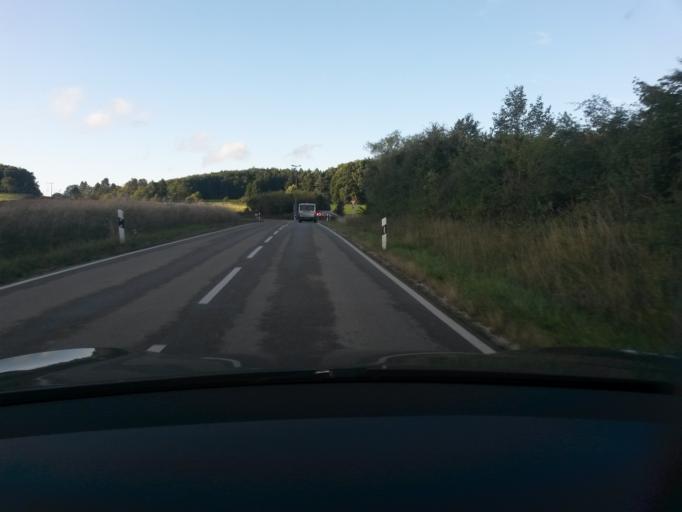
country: DE
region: Bavaria
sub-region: Upper Palatinate
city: Hohenfels
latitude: 49.1827
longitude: 11.8184
